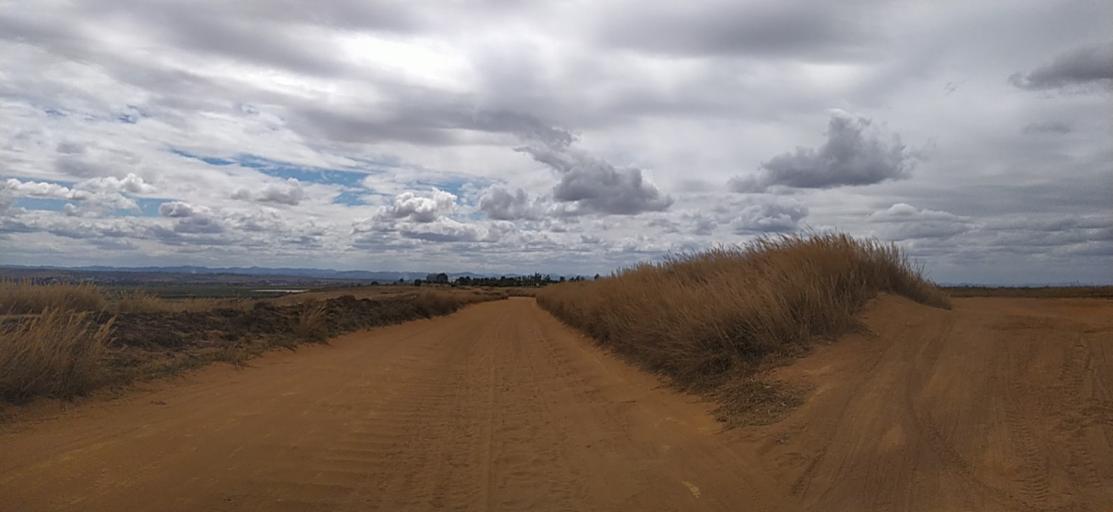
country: MG
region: Alaotra Mangoro
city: Ambatondrazaka
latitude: -17.9063
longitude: 48.2610
